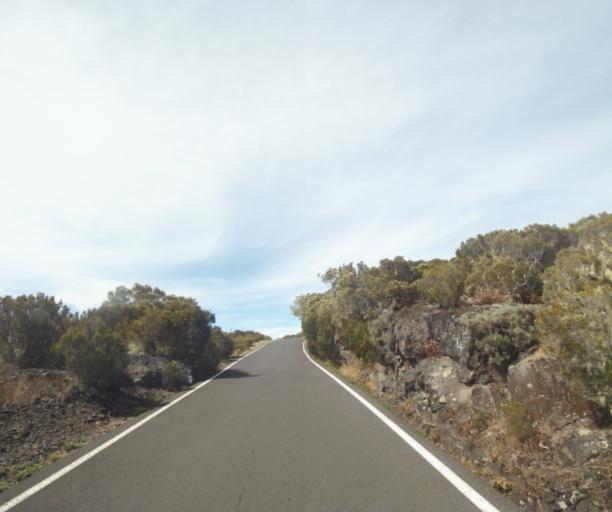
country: RE
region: Reunion
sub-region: Reunion
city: Trois-Bassins
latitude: -21.0727
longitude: 55.3819
